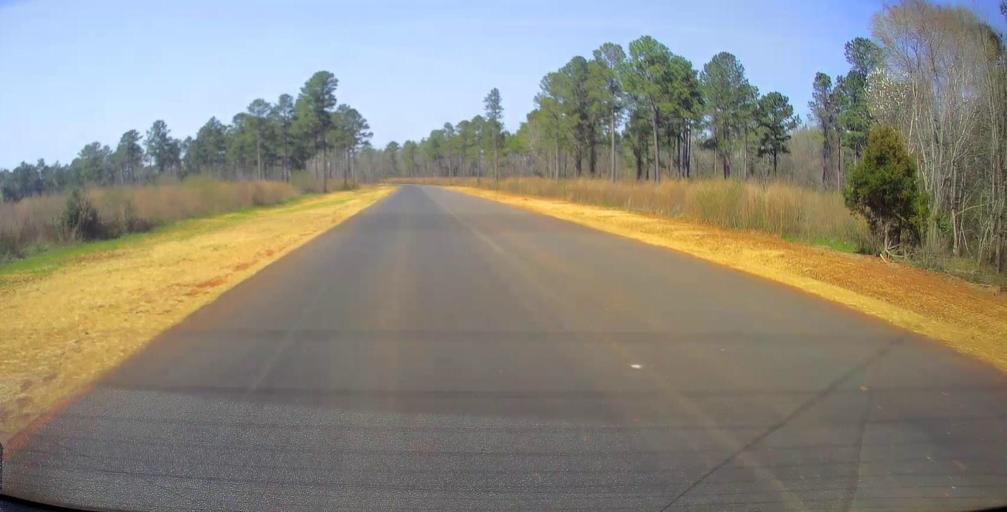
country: US
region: Georgia
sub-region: Houston County
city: Centerville
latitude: 32.5997
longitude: -83.7289
